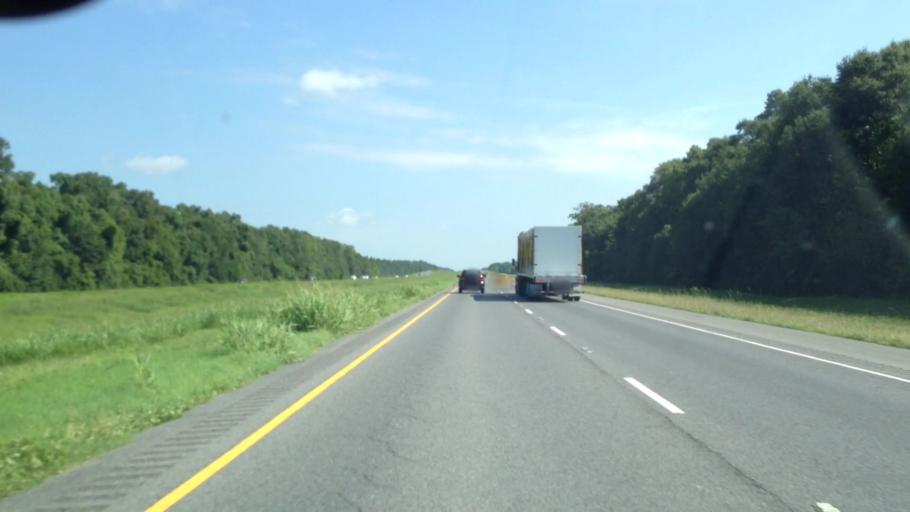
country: US
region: Louisiana
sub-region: Avoyelles Parish
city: Bunkie
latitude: 30.8546
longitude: -92.2282
